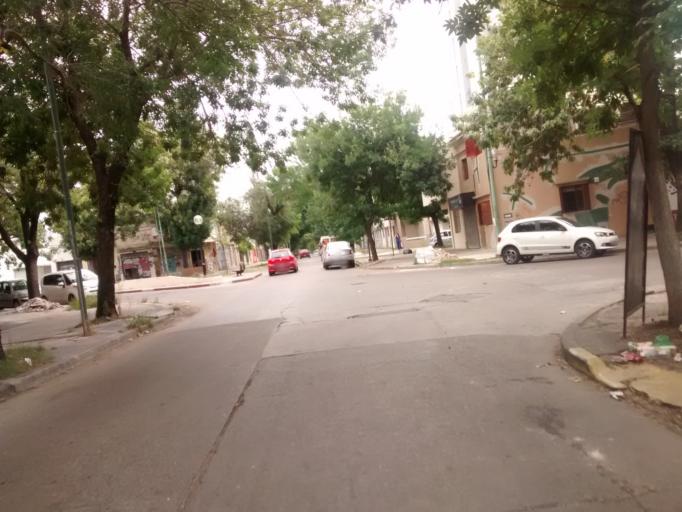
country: AR
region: Buenos Aires
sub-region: Partido de La Plata
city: La Plata
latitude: -34.9313
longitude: -57.9459
